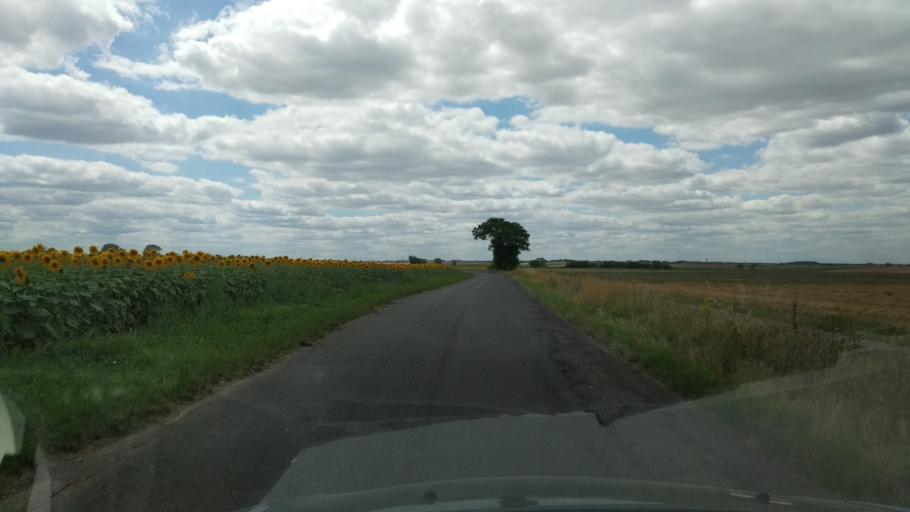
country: FR
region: Poitou-Charentes
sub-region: Departement de la Vienne
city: Avanton
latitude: 46.6739
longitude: 0.3357
